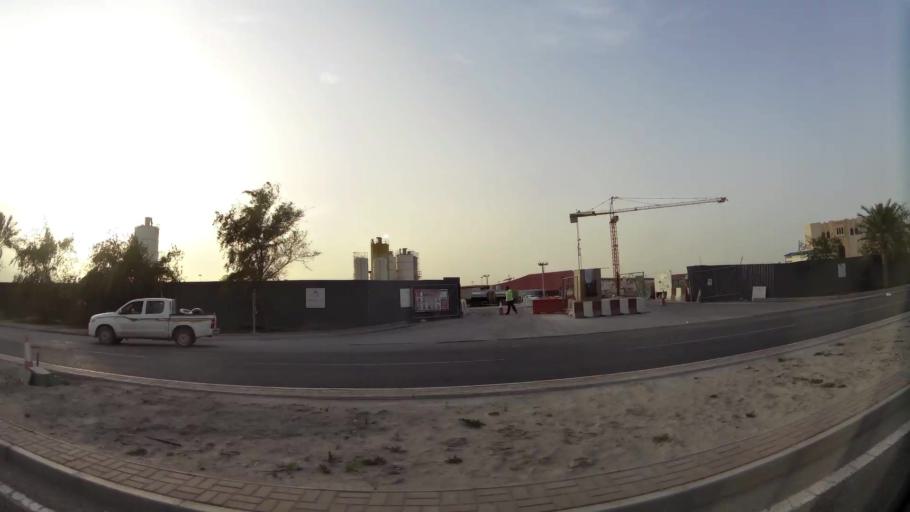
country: QA
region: Baladiyat ad Dawhah
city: Doha
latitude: 25.3471
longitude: 51.5246
